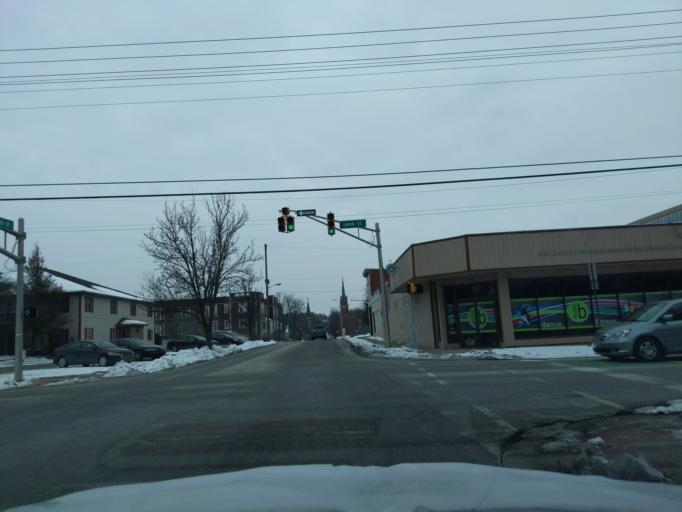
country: US
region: Indiana
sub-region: Tippecanoe County
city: Lafayette
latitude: 40.4249
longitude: -86.8870
